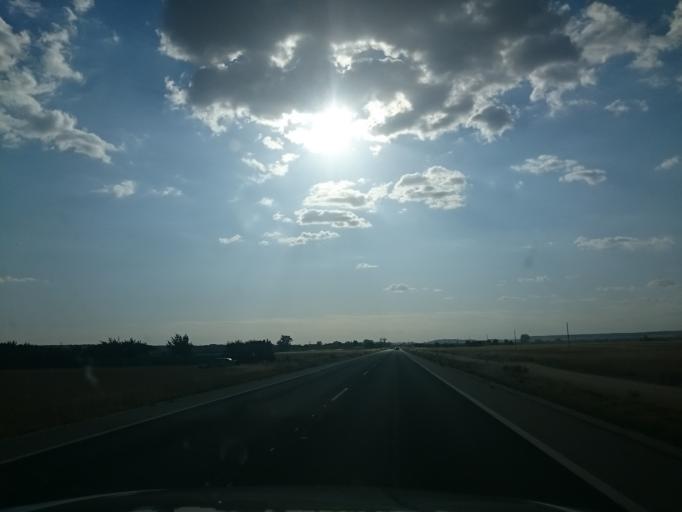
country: ES
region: Castille and Leon
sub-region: Provincia de Burgos
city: Los Tomillares
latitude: 42.3370
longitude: -3.5870
